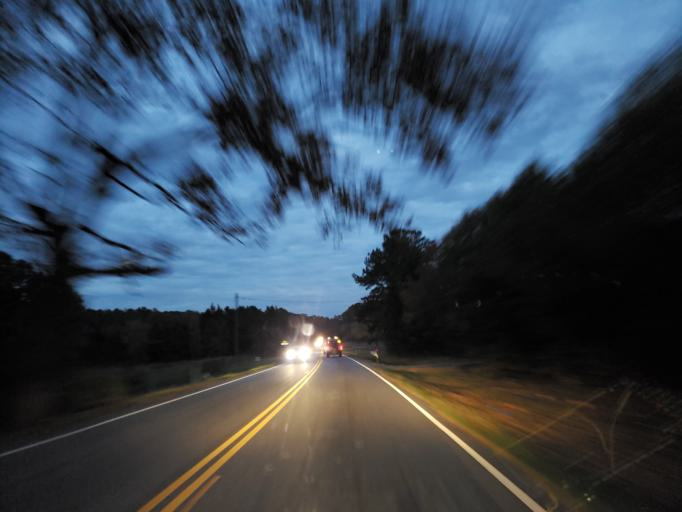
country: US
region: Georgia
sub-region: Cobb County
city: Powder Springs
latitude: 33.9079
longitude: -84.6797
